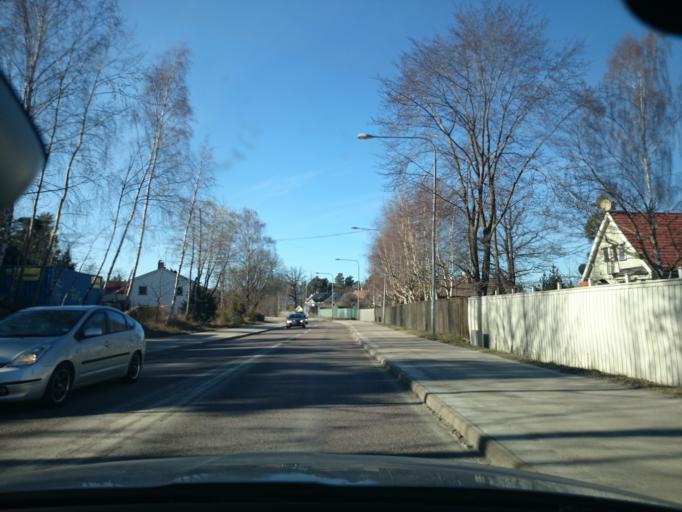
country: SE
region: Stockholm
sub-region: Huddinge Kommun
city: Huddinge
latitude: 59.2580
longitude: 17.9791
